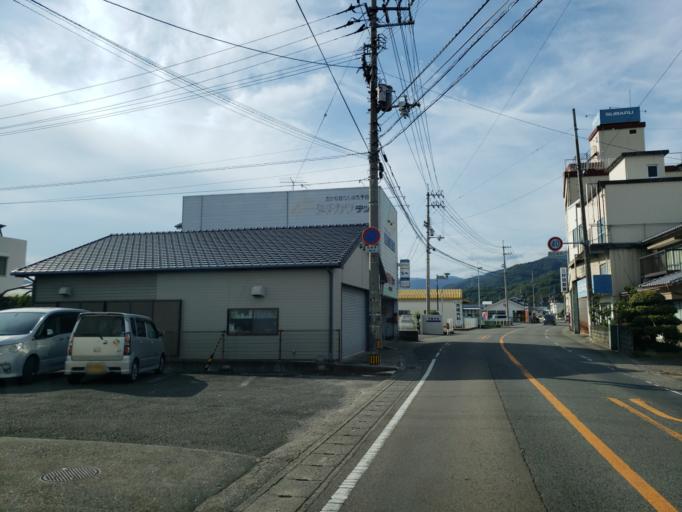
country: JP
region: Tokushima
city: Wakimachi
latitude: 34.0695
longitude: 134.1441
